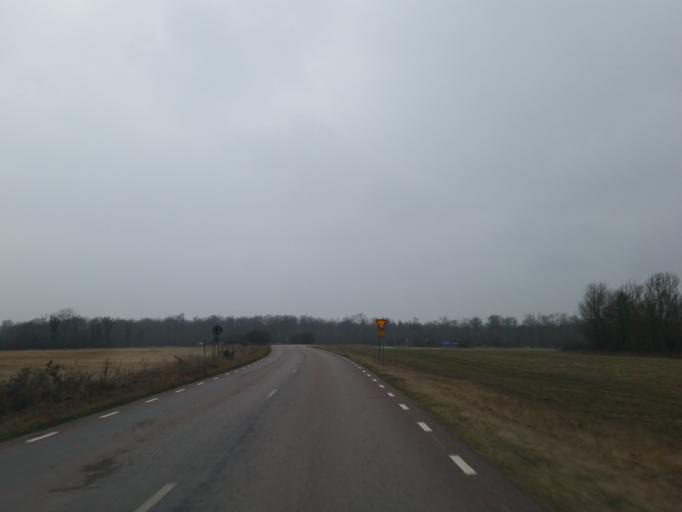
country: SE
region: Kalmar
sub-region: Morbylanga Kommun
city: Sodra Sandby
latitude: 56.6521
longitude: 16.5629
